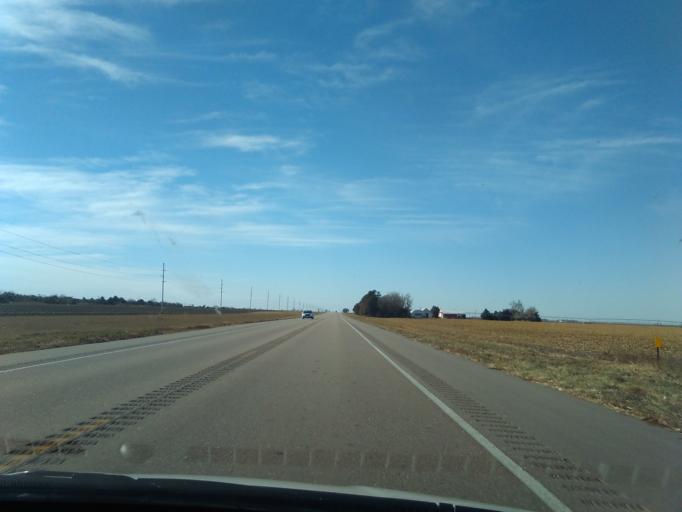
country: US
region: Nebraska
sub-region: Clay County
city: Harvard
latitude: 40.5828
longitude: -98.1577
